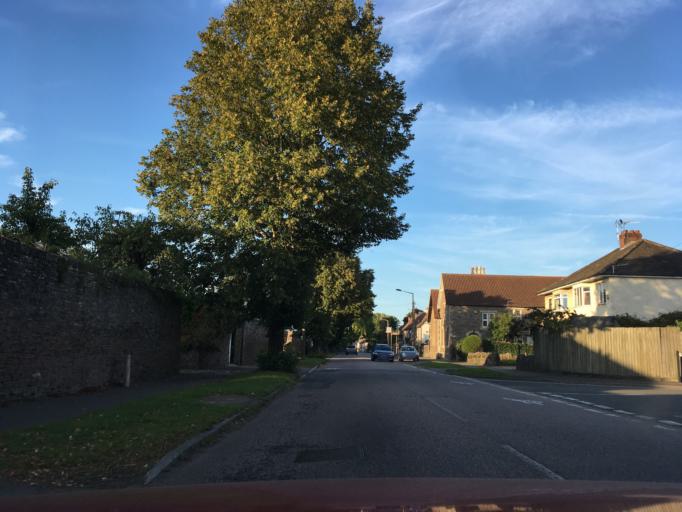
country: GB
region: England
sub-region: South Gloucestershire
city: Winterbourne
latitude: 51.5256
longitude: -2.5069
